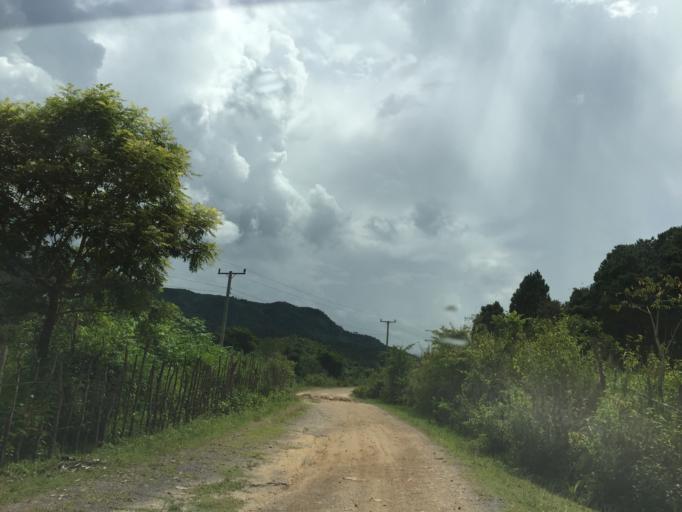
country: LA
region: Xiangkhoang
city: Muang Phonsavan
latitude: 19.3423
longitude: 103.5549
